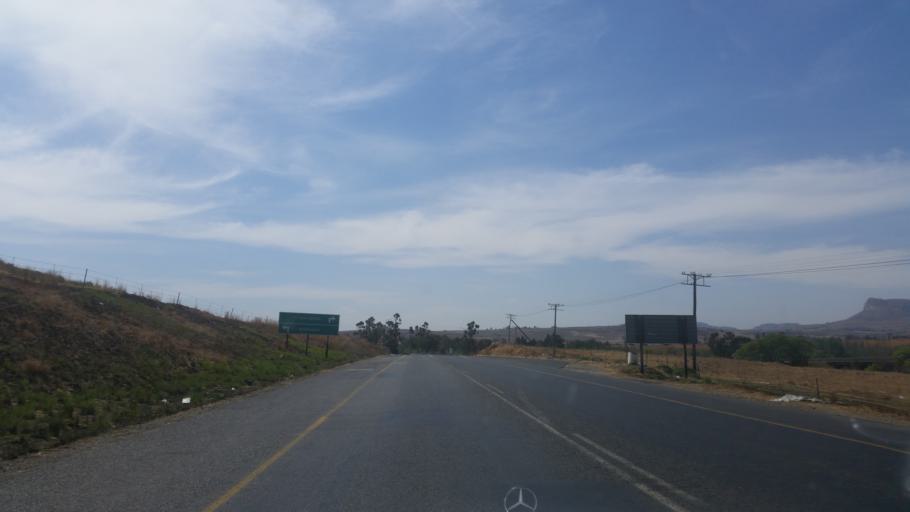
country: ZA
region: Orange Free State
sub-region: Thabo Mofutsanyana District Municipality
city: Harrismith
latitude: -28.2920
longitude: 29.0885
